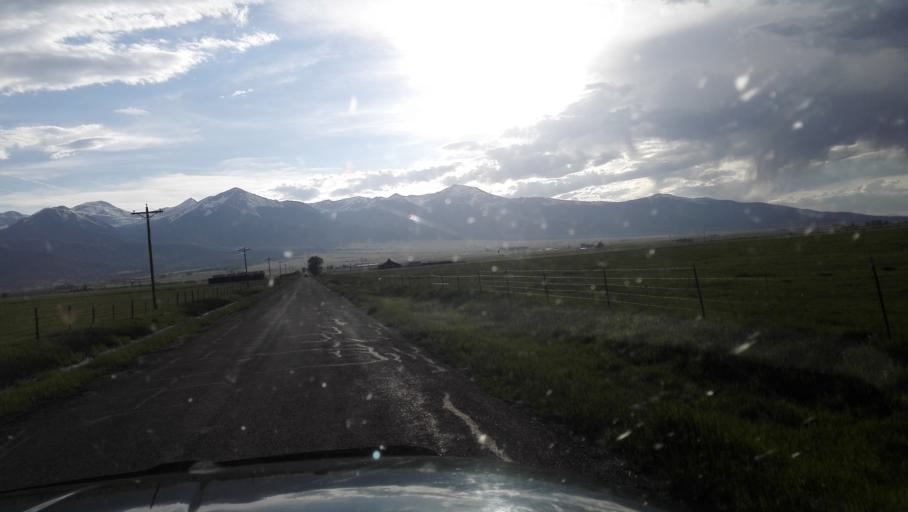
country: US
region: Colorado
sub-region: Custer County
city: Westcliffe
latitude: 38.1316
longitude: -105.4917
